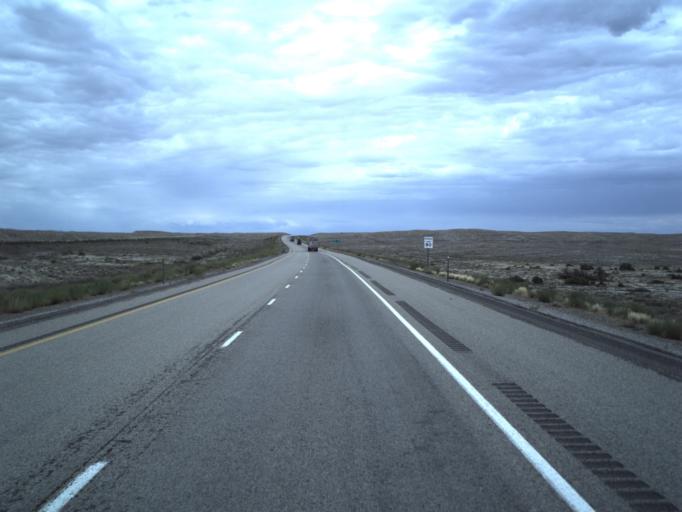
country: US
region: Utah
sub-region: Grand County
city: Moab
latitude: 38.9824
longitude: -109.3420
